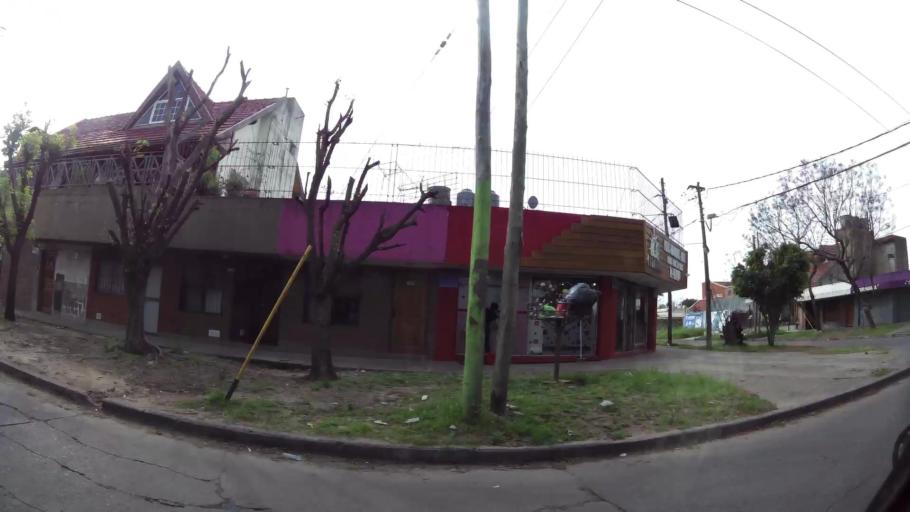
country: AR
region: Buenos Aires
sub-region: Partido de Quilmes
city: Quilmes
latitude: -34.7555
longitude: -58.2766
